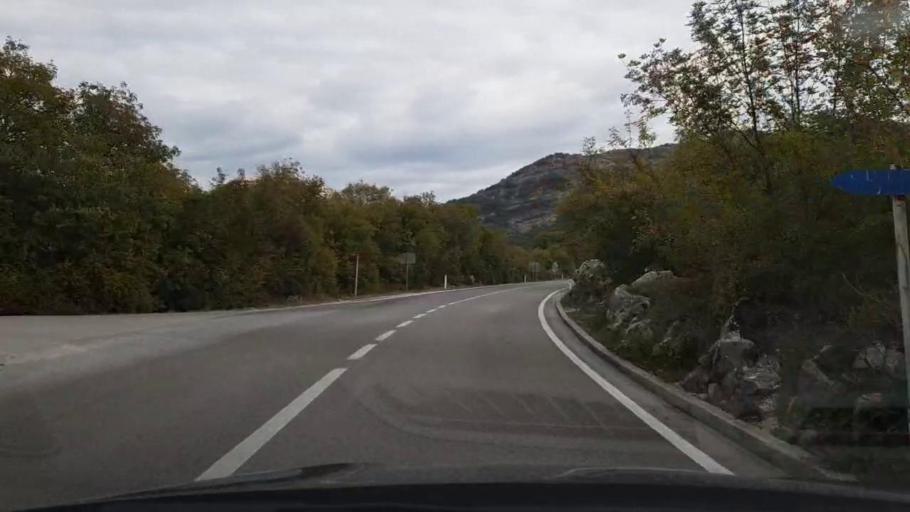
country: BA
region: Republika Srpska
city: Trebinje
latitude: 42.6896
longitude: 18.2567
